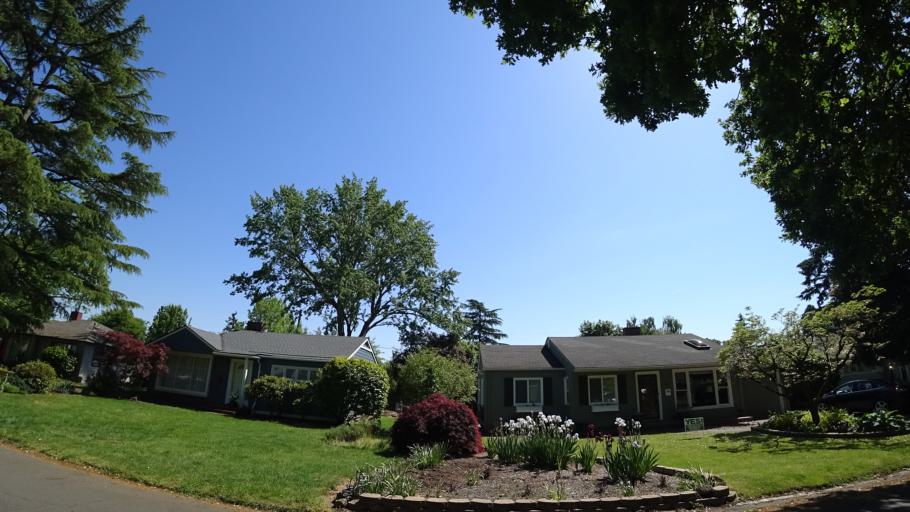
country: US
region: Oregon
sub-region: Washington County
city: Cedar Hills
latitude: 45.4979
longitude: -122.8028
